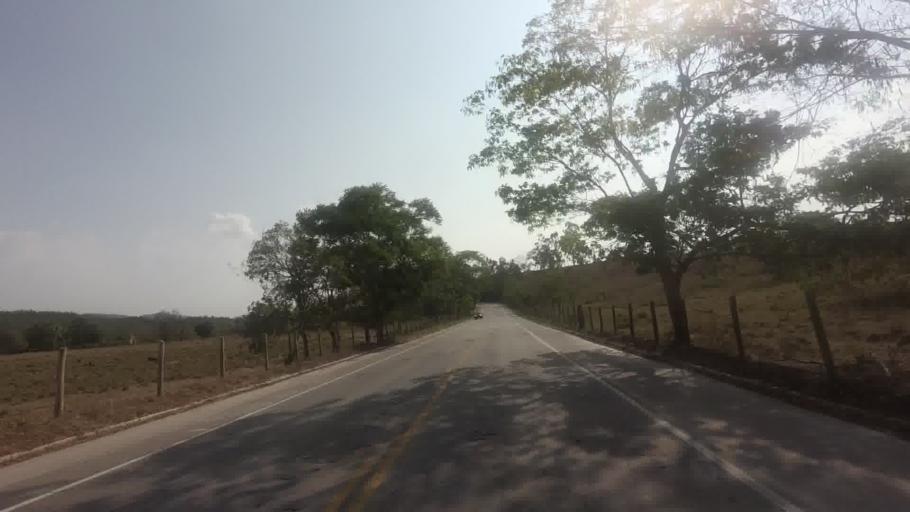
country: BR
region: Rio de Janeiro
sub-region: Bom Jesus Do Itabapoana
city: Bom Jesus do Itabapoana
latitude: -21.1475
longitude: -41.5884
